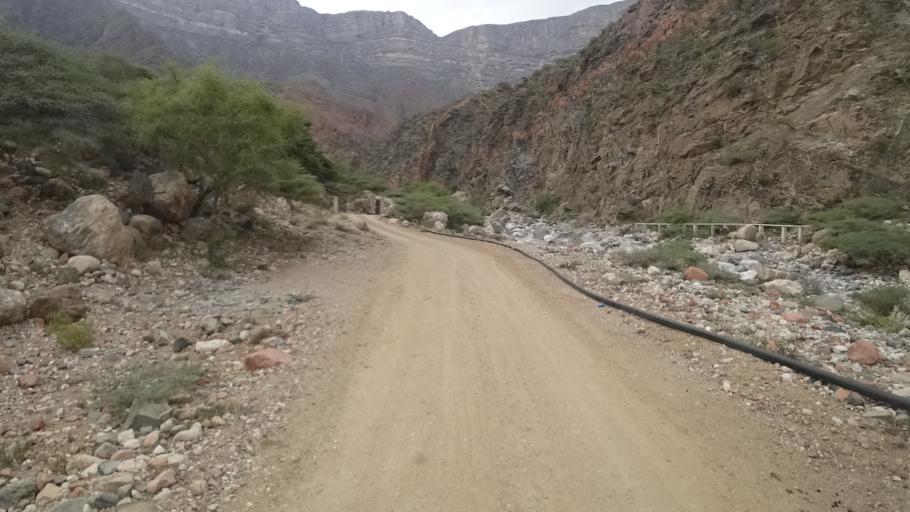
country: OM
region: Zufar
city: Salalah
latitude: 17.1850
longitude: 54.9439
